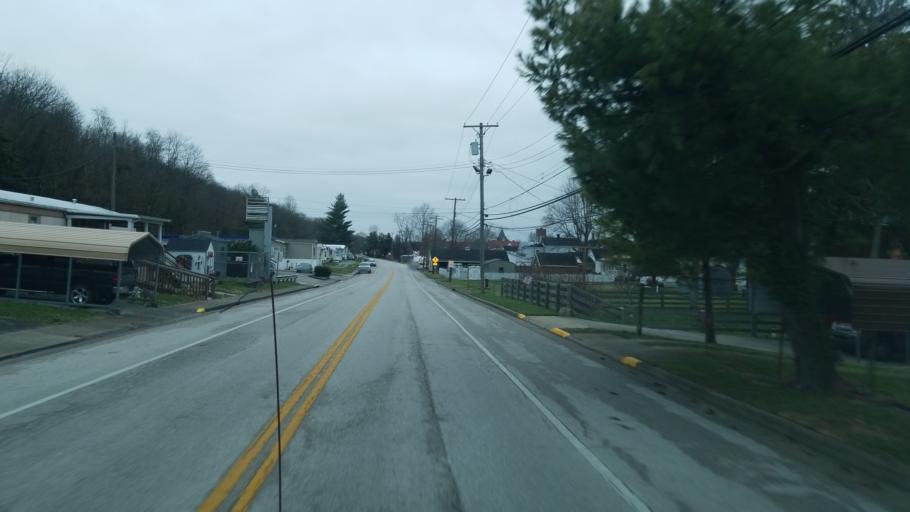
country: US
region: Kentucky
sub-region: Bracken County
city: Augusta
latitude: 38.7711
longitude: -84.0018
